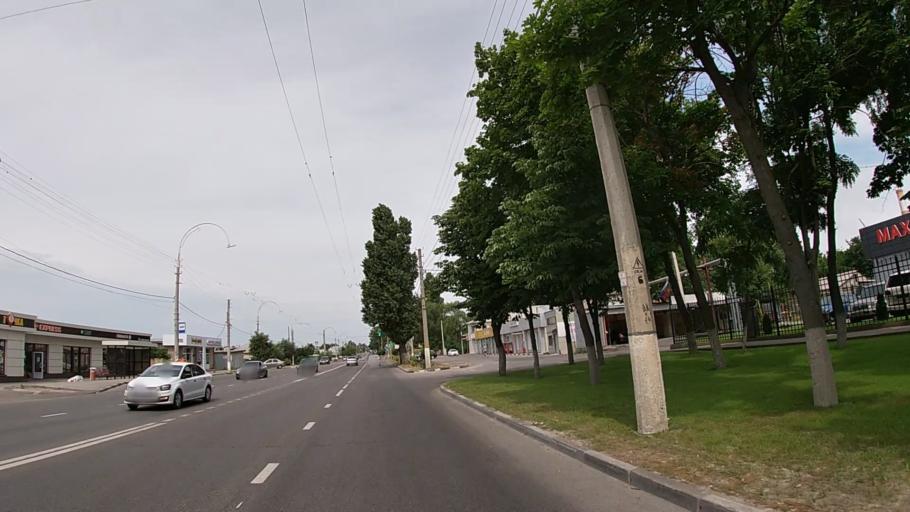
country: RU
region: Belgorod
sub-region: Belgorodskiy Rayon
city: Belgorod
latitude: 50.6050
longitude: 36.5558
